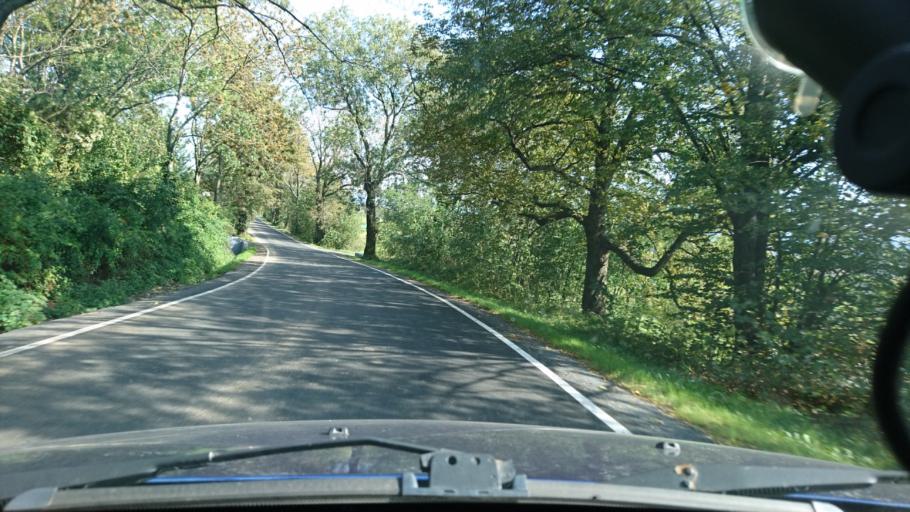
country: PL
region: Silesian Voivodeship
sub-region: Powiat cieszynski
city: Pogorze
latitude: 49.8163
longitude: 18.8589
